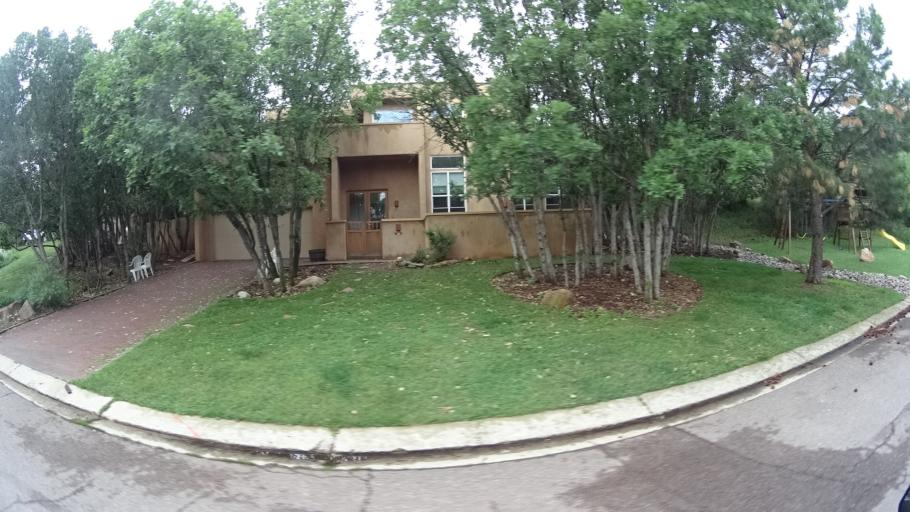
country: US
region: Colorado
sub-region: El Paso County
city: Manitou Springs
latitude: 38.8498
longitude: -104.8957
